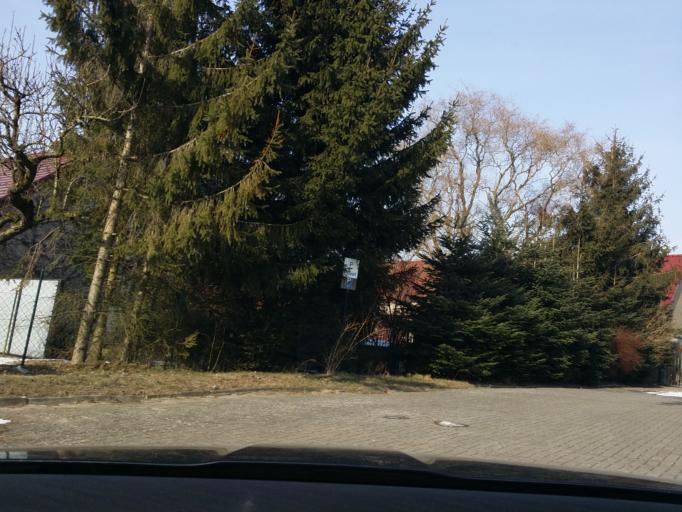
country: DE
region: Brandenburg
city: Pritzwalk
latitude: 53.1407
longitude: 12.2333
